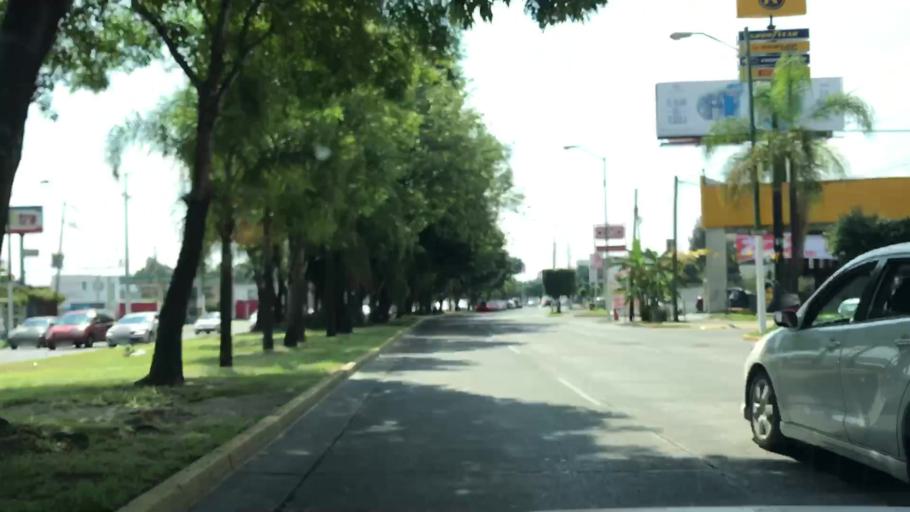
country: MX
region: Jalisco
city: Guadalajara
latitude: 20.6520
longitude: -103.4226
